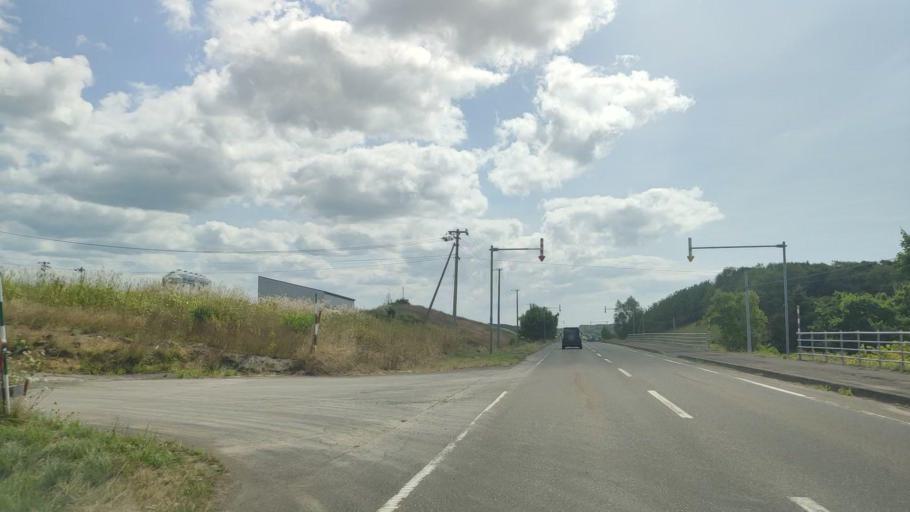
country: JP
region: Hokkaido
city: Makubetsu
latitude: 44.7815
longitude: 141.7908
